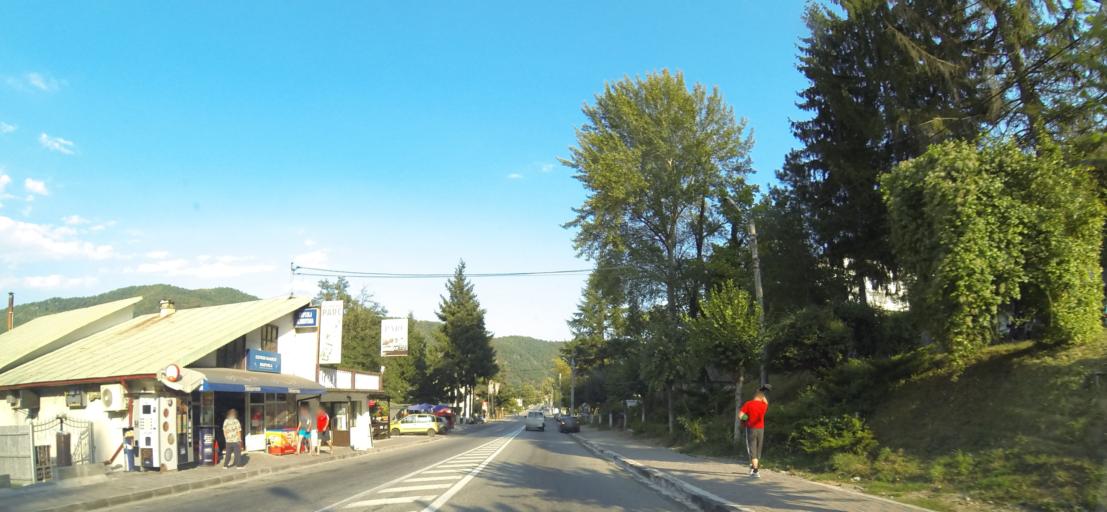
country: RO
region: Valcea
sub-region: Oras Calimanesti
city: Calimanesti
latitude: 45.2598
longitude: 24.3210
